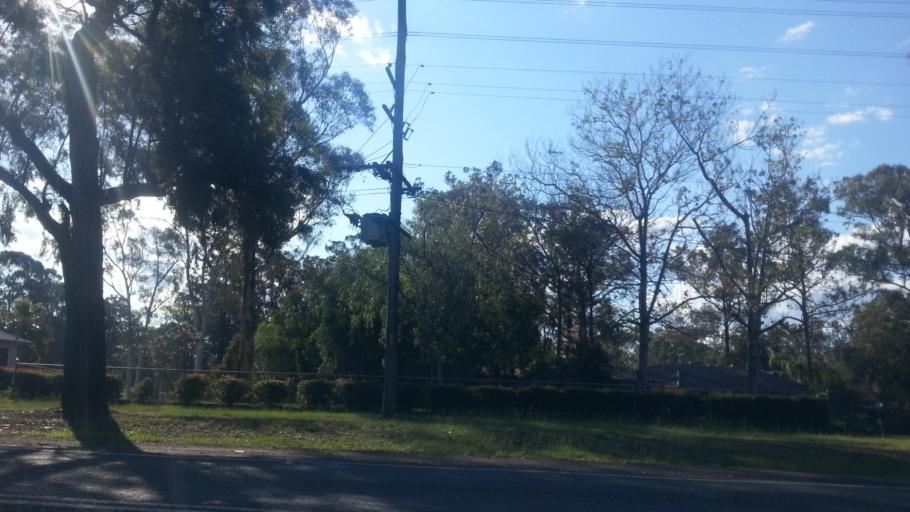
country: AU
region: New South Wales
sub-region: Hawkesbury
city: Richmond
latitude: -33.6710
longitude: 150.7522
